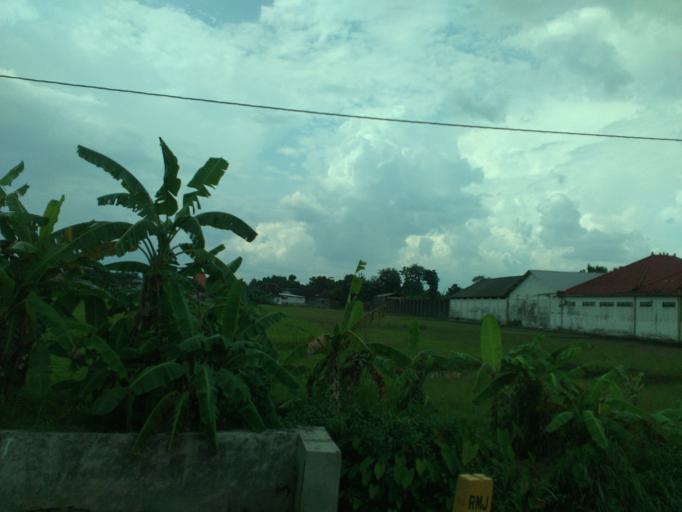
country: ID
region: Central Java
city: Ceper
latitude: -7.6672
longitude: 110.6619
